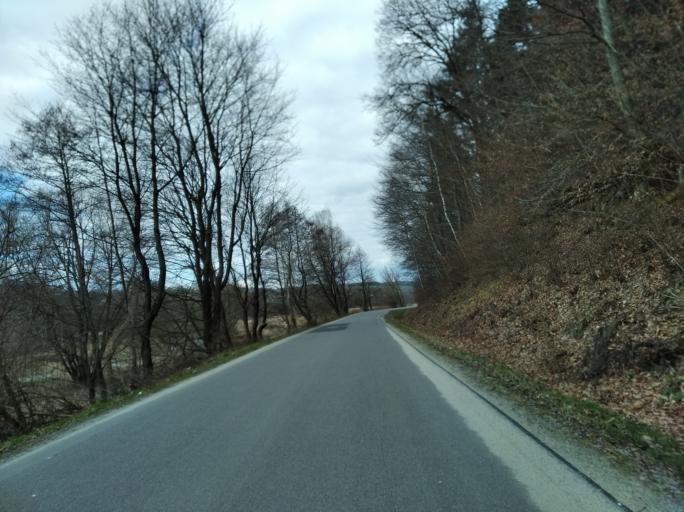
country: PL
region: Subcarpathian Voivodeship
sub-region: Powiat strzyzowski
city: Frysztak
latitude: 49.8531
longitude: 21.6246
